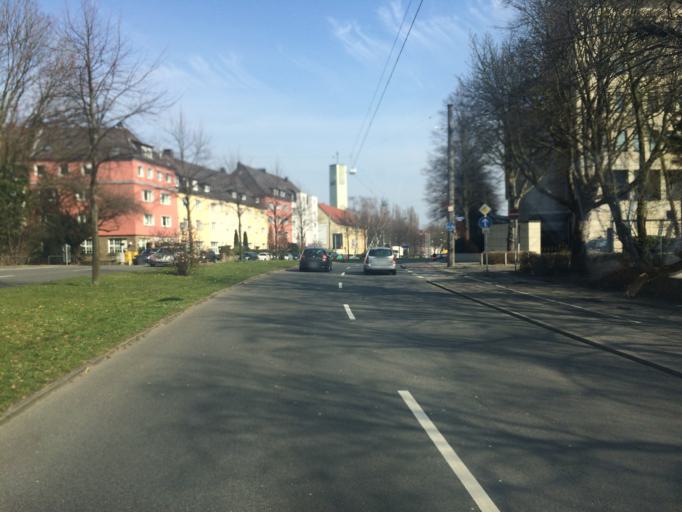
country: DE
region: North Rhine-Westphalia
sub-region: Regierungsbezirk Arnsberg
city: Dortmund
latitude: 51.4989
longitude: 7.4501
